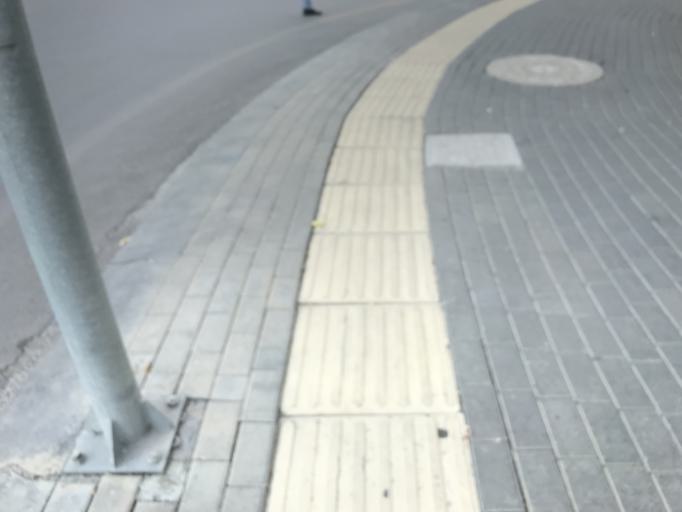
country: TR
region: Ankara
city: Ankara
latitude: 39.9172
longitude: 32.8248
